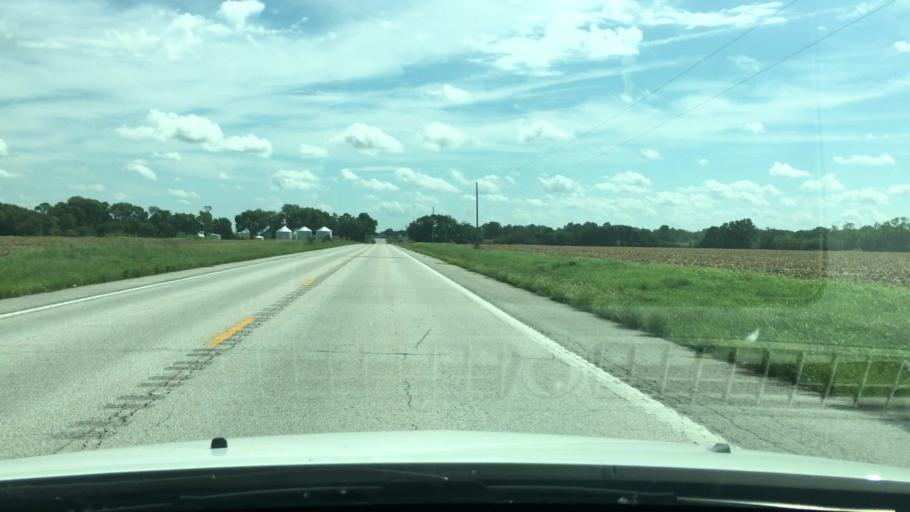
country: US
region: Missouri
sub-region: Audrain County
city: Vandalia
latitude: 39.2796
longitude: -91.5899
